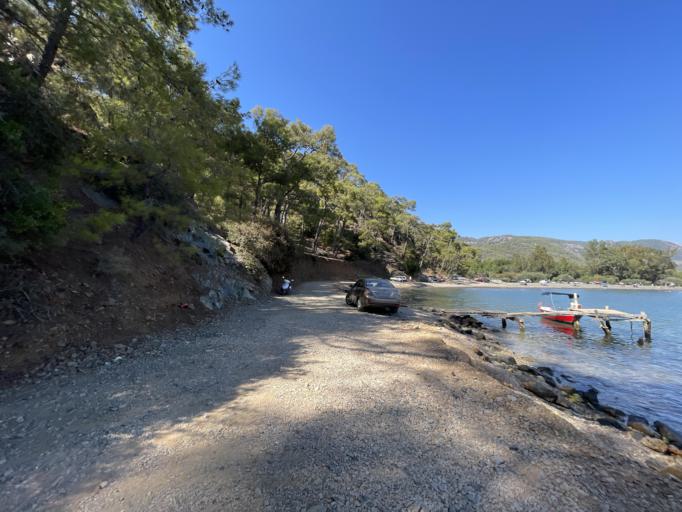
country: TR
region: Mugla
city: Goecek
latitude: 36.7292
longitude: 28.9649
